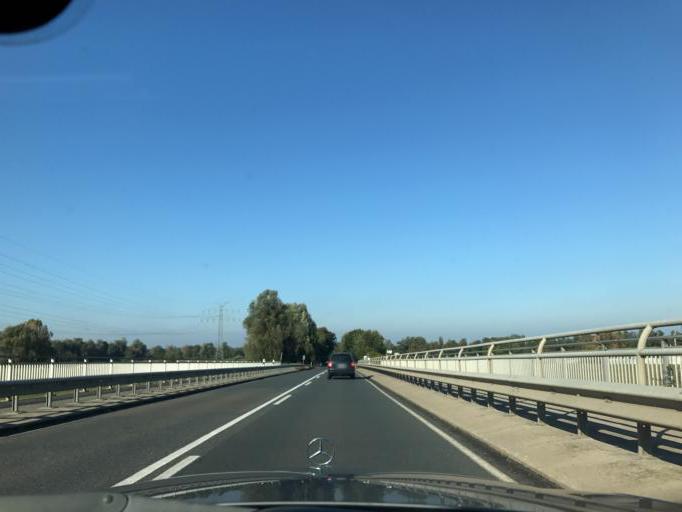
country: DE
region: Lower Saxony
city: Weener
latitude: 53.1045
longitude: 7.3515
